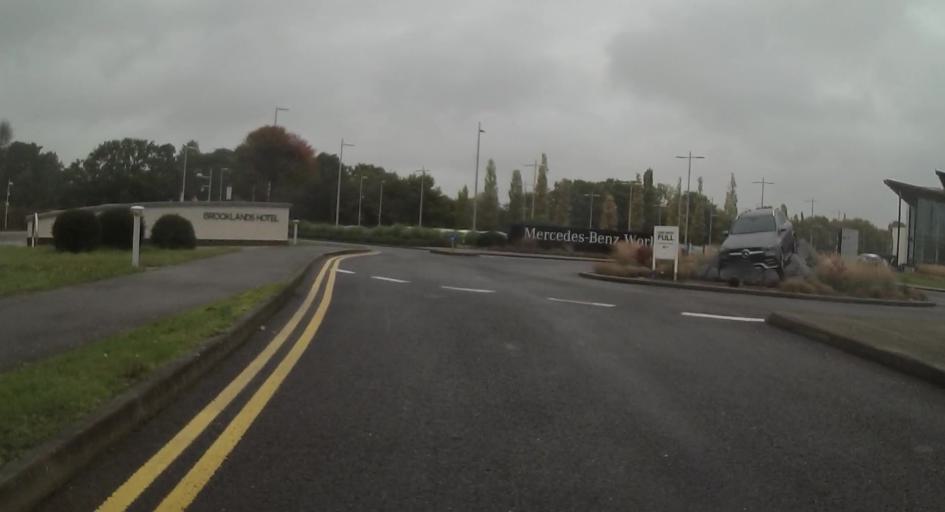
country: GB
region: England
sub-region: Surrey
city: Byfleet
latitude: 51.3535
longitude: -0.4698
